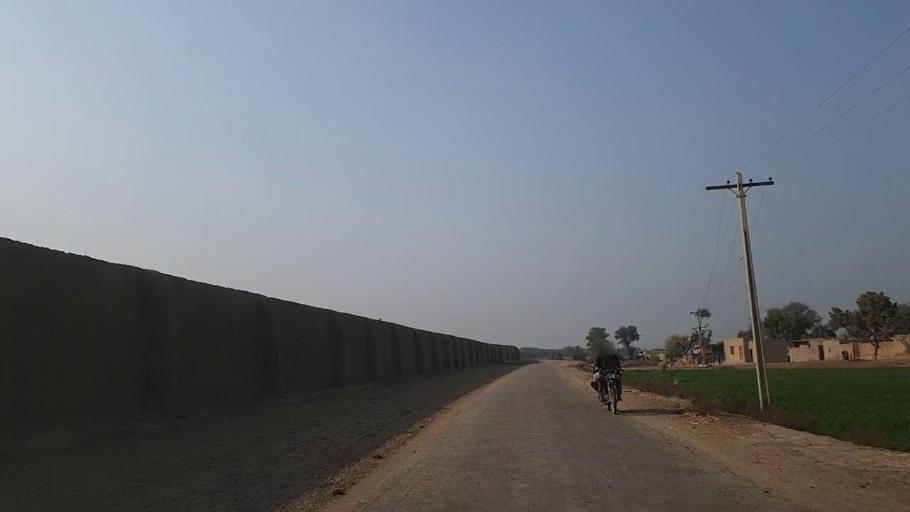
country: PK
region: Sindh
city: Sann
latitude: 26.1052
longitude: 68.1779
